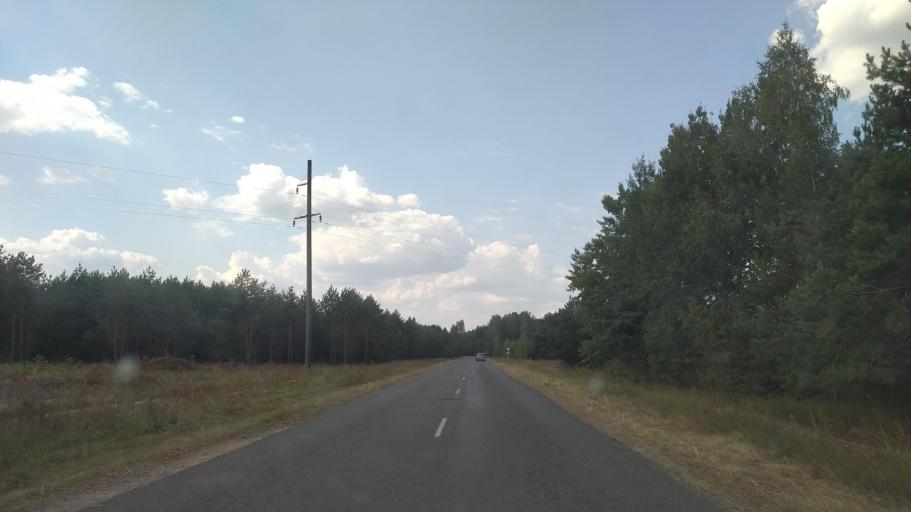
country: BY
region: Brest
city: Drahichyn
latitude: 52.1054
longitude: 25.1202
